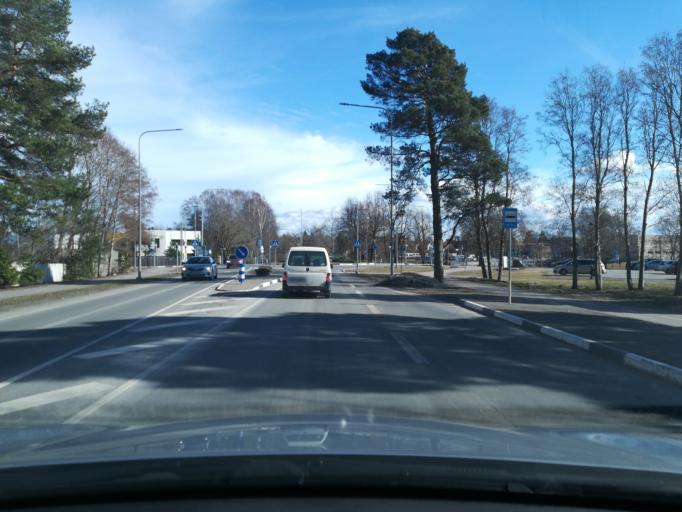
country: EE
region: Harju
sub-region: Saue vald
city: Laagri
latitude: 59.3536
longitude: 24.6072
